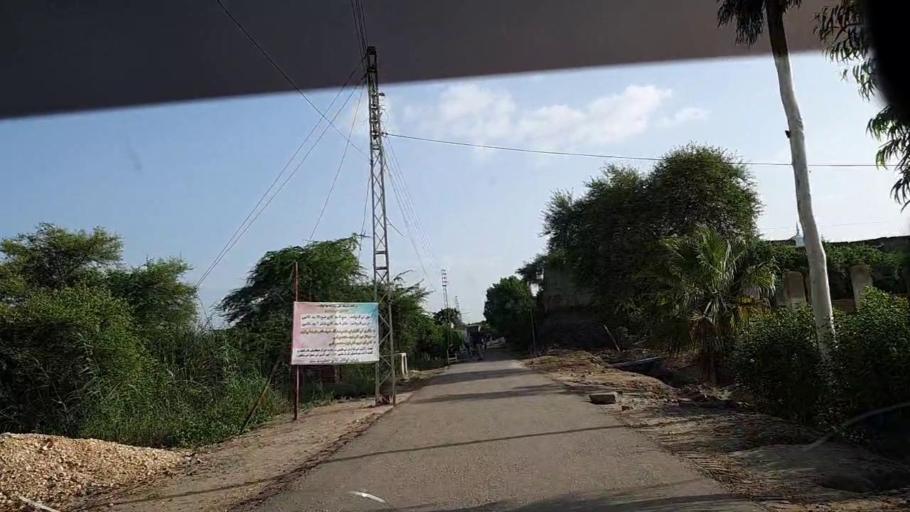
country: PK
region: Sindh
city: Badin
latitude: 24.5632
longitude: 68.9026
